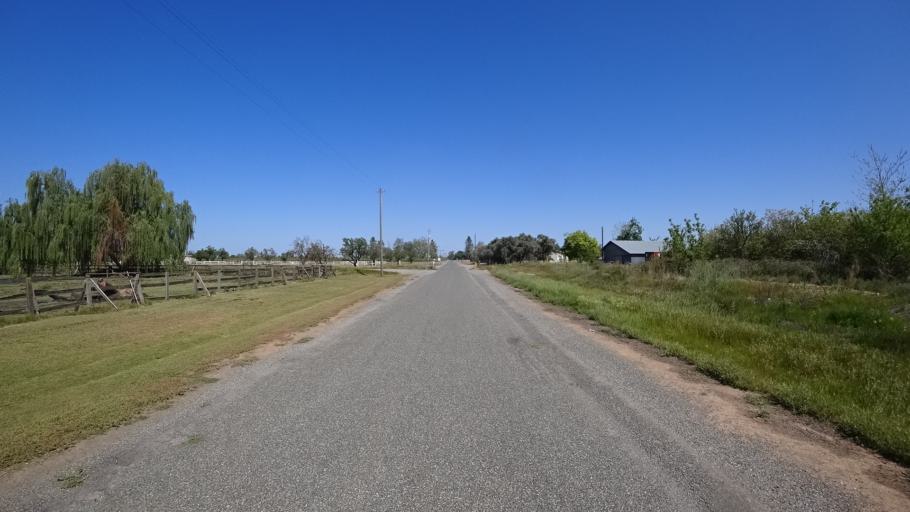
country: US
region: California
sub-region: Glenn County
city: Orland
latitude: 39.7819
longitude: -122.1597
